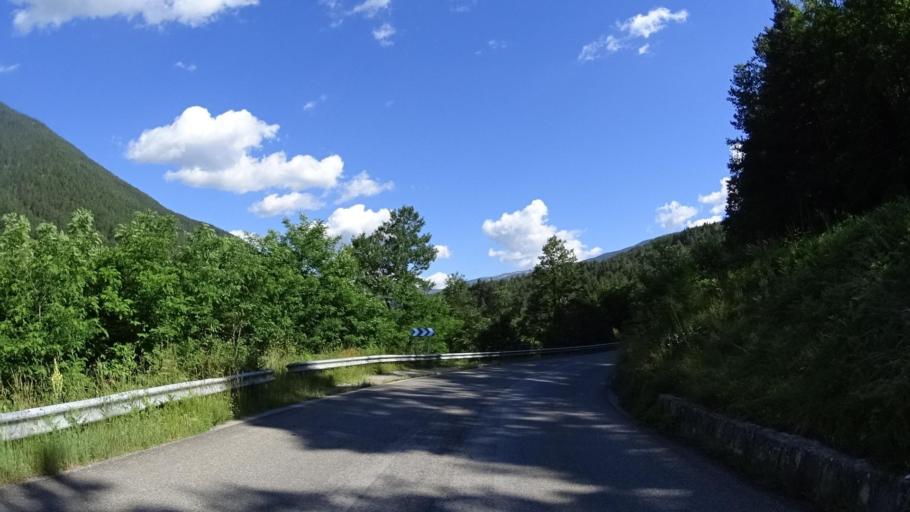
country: FR
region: Provence-Alpes-Cote d'Azur
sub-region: Departement des Alpes-de-Haute-Provence
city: Annot
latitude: 43.9883
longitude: 6.6475
